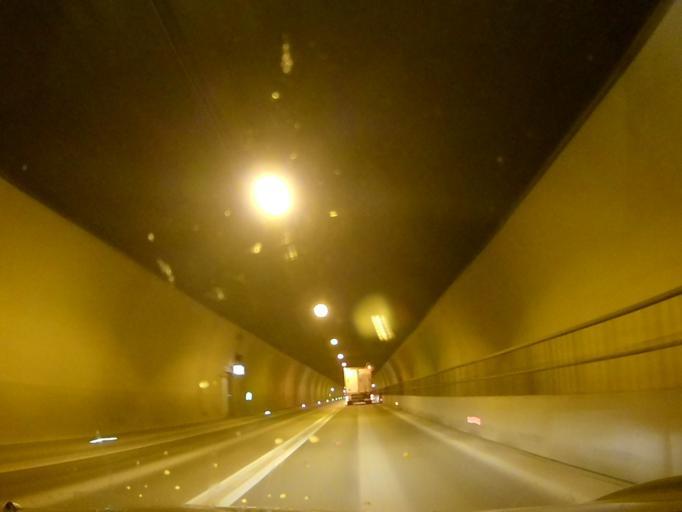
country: AT
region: Salzburg
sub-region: Politischer Bezirk Zell am See
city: Lend
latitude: 47.2867
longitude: 13.0658
